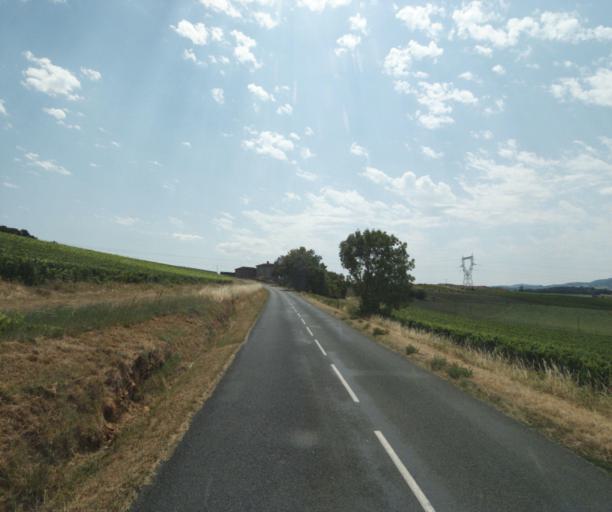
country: FR
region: Rhone-Alpes
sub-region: Departement du Rhone
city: Chatillon
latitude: 45.8718
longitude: 4.6039
